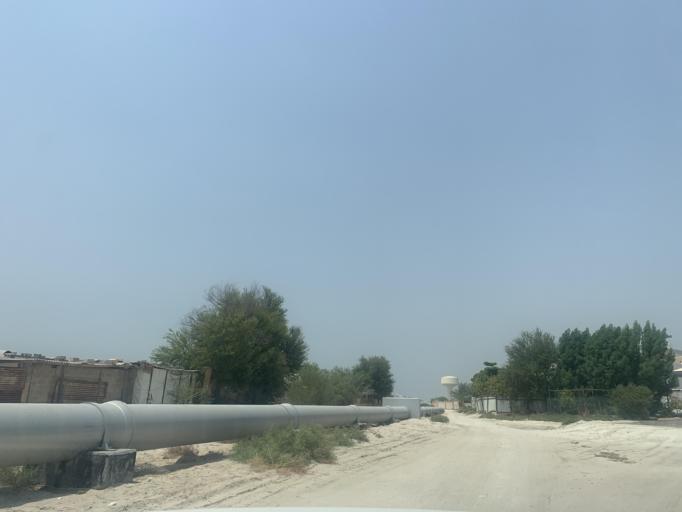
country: BH
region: Central Governorate
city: Madinat Hamad
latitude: 26.1426
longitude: 50.4666
